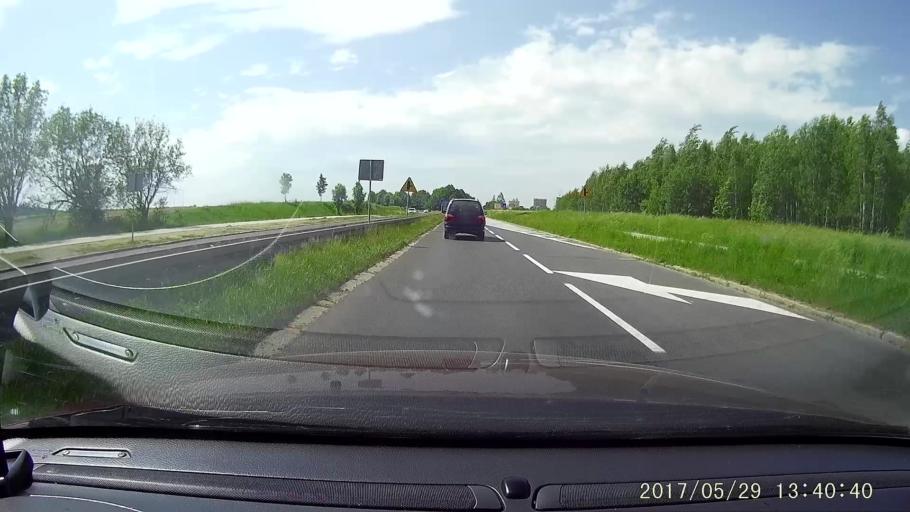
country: PL
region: Lower Silesian Voivodeship
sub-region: Powiat lubanski
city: Luban
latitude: 51.1328
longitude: 15.2712
